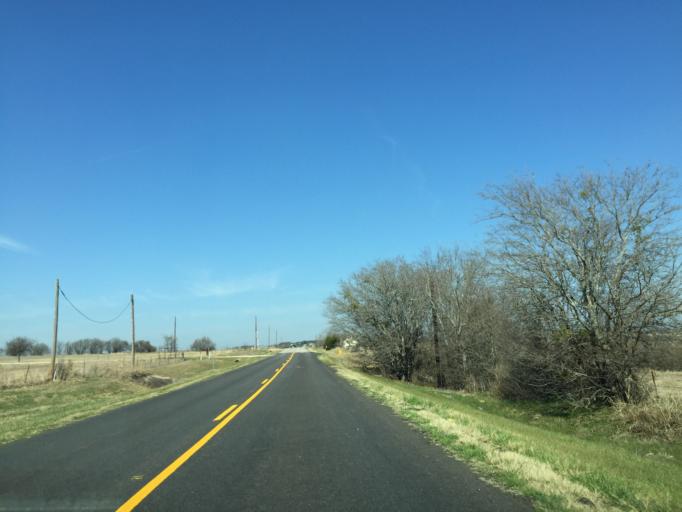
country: US
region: Texas
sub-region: Williamson County
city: Serenada
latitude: 30.7199
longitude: -97.5810
